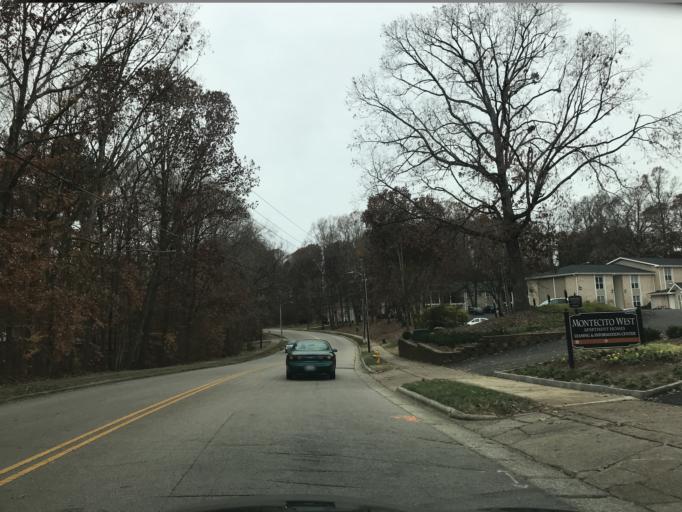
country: US
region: North Carolina
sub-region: Wake County
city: Raleigh
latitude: 35.8372
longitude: -78.6161
